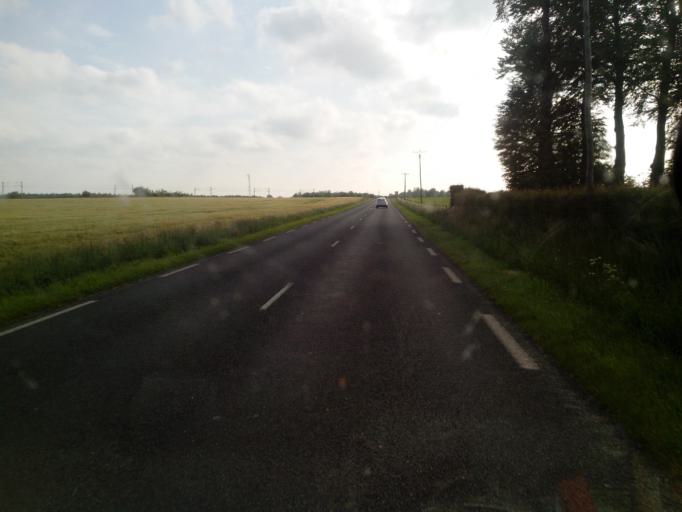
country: FR
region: Haute-Normandie
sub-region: Departement de la Seine-Maritime
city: Sainte-Marie-des-Champs
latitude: 49.6358
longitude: 0.8186
